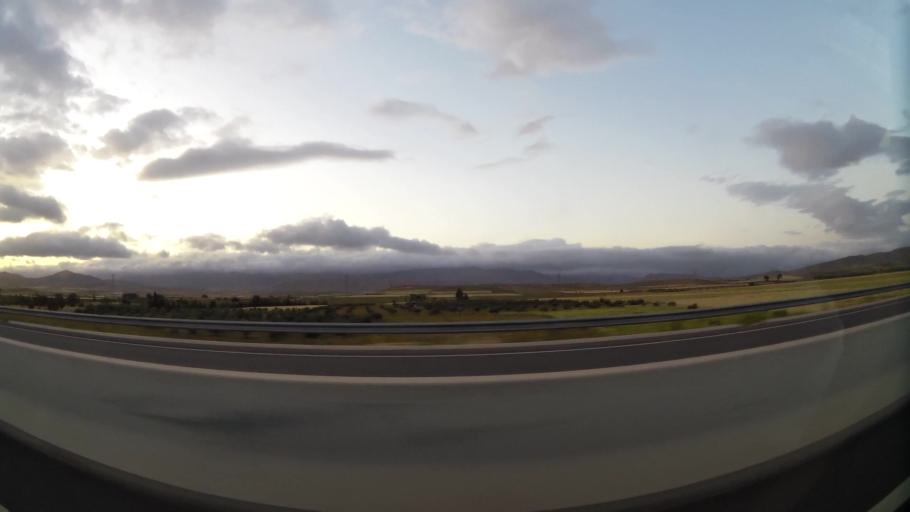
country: MA
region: Oriental
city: El Aioun
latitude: 34.6262
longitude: -2.5227
